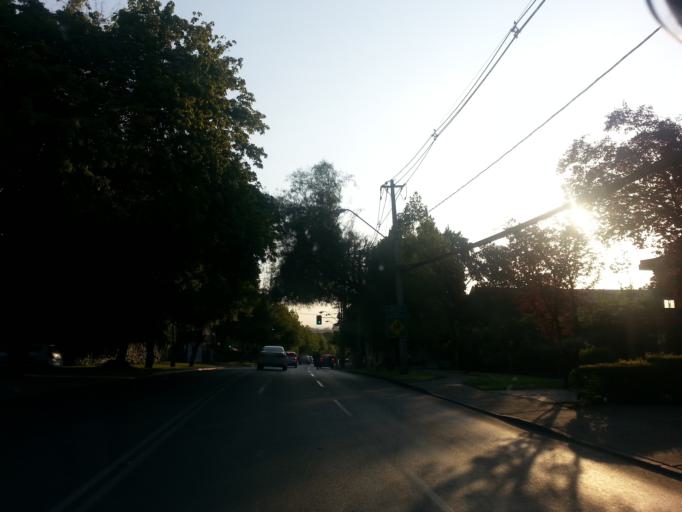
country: CL
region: Santiago Metropolitan
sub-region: Provincia de Santiago
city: Villa Presidente Frei, Nunoa, Santiago, Chile
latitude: -33.4034
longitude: -70.5351
